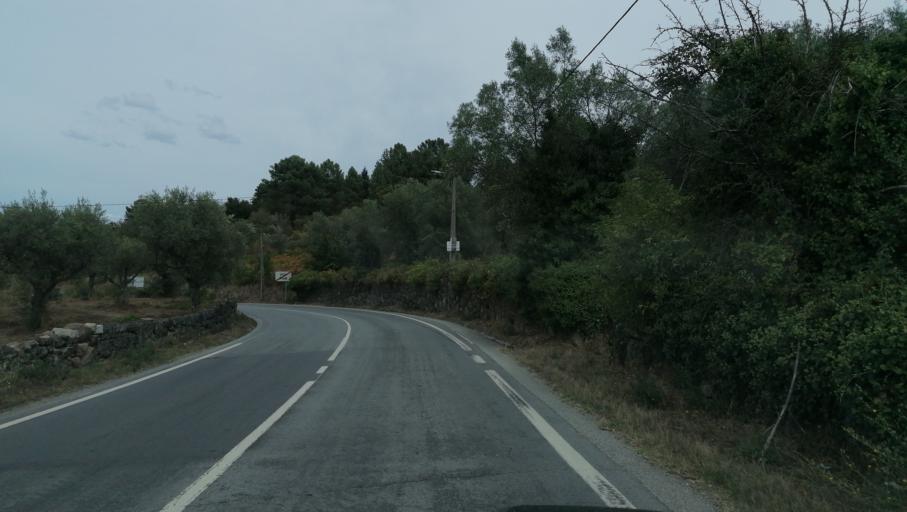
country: PT
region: Vila Real
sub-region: Vila Pouca de Aguiar
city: Vila Pouca de Aguiar
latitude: 41.5305
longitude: -7.6114
